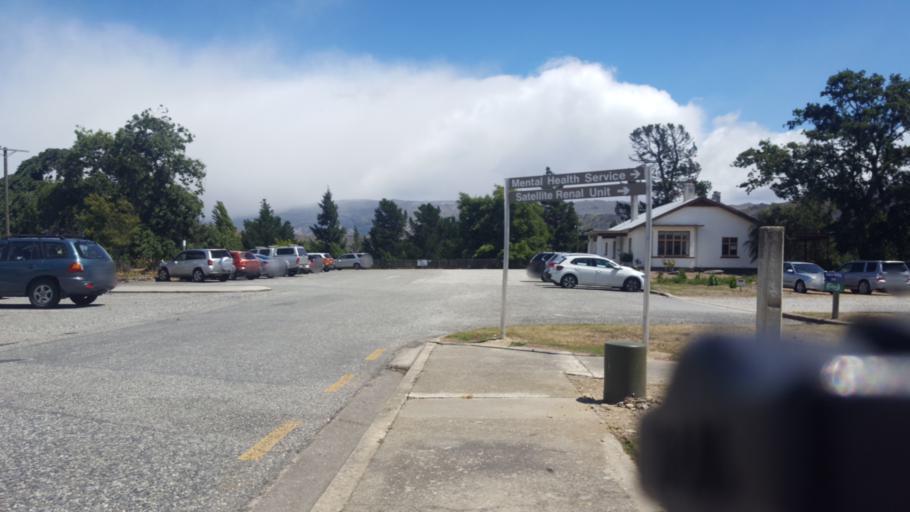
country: NZ
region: Otago
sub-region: Queenstown-Lakes District
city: Wanaka
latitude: -45.2005
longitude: 169.3298
